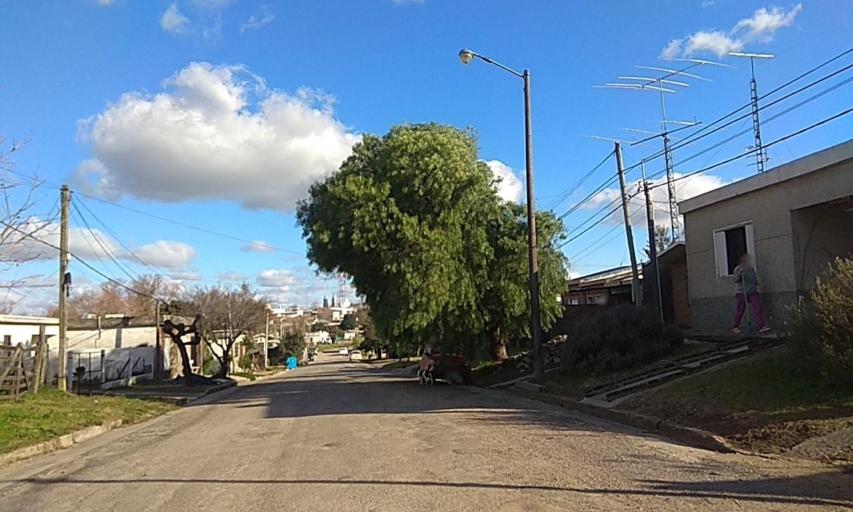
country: UY
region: Florida
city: Florida
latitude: -34.0906
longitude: -56.2105
